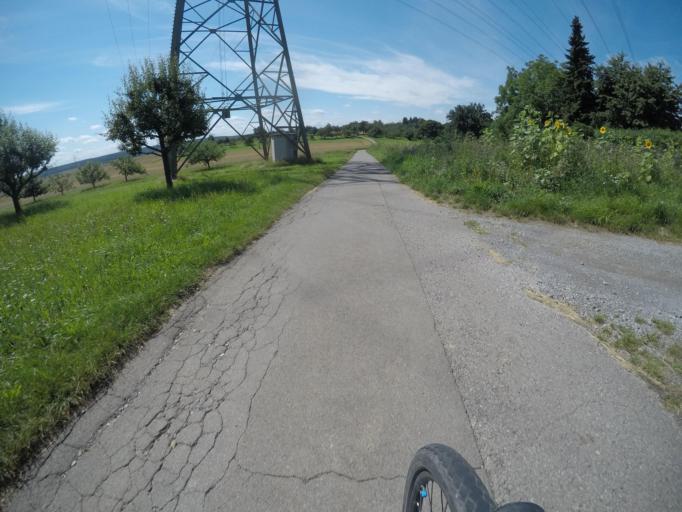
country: DE
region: Baden-Wuerttemberg
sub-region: Regierungsbezirk Stuttgart
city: Gartringen
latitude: 48.6581
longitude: 8.9066
